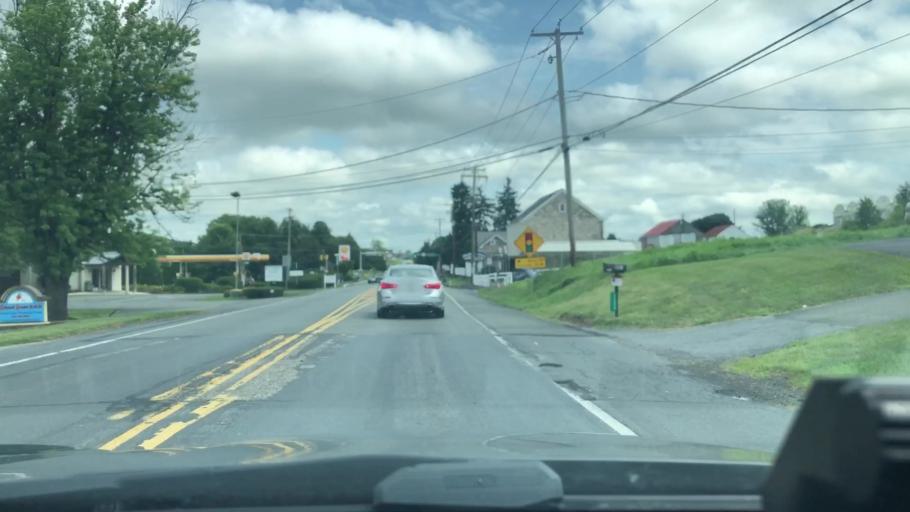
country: US
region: Pennsylvania
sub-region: Berks County
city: Bally
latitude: 40.3829
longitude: -75.6047
